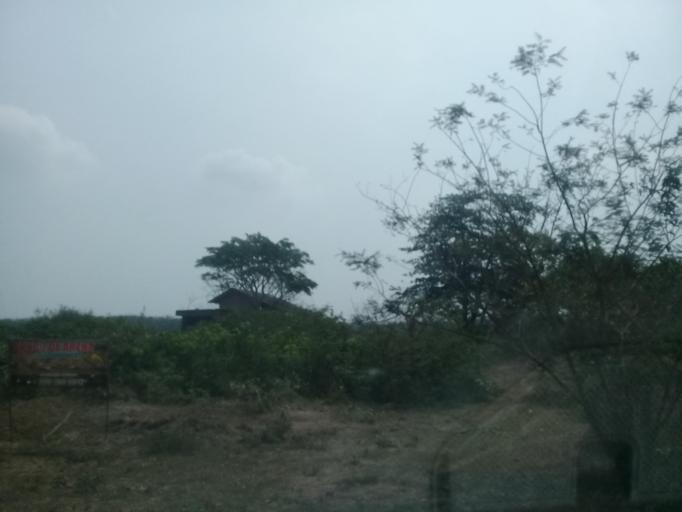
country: MX
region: Veracruz
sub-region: Veracruz
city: Fraccionamiento Geovillas los Pinos
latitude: 19.2353
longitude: -96.2405
